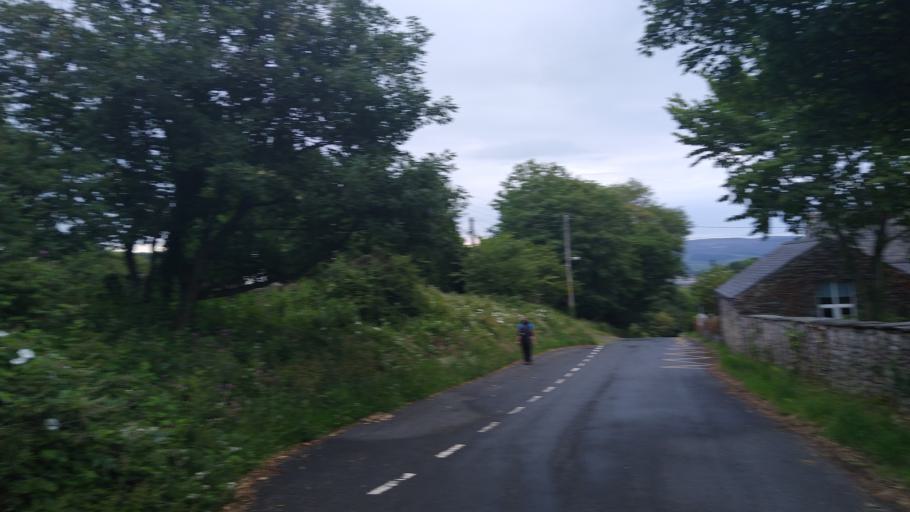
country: GB
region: England
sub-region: Cumbria
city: Millom
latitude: 54.2584
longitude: -3.2626
